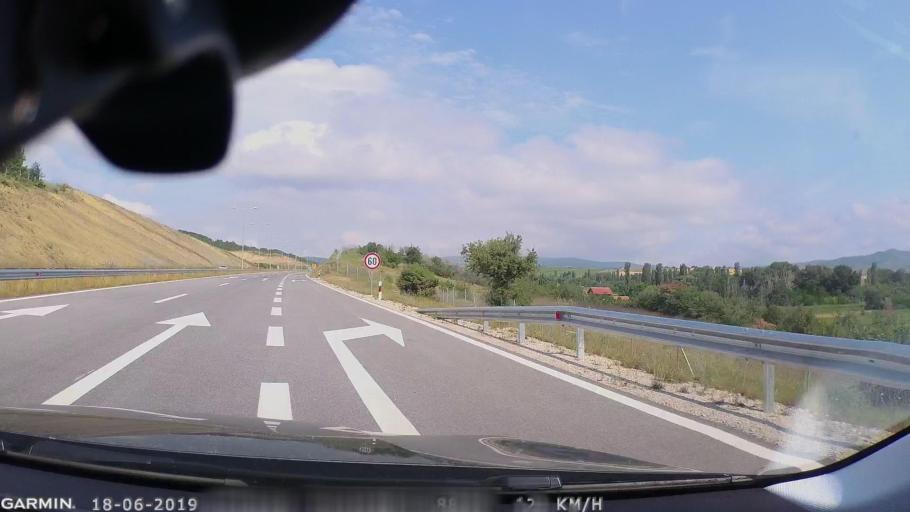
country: MK
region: Sveti Nikole
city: Gorobinci
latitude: 41.9139
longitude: 21.8893
